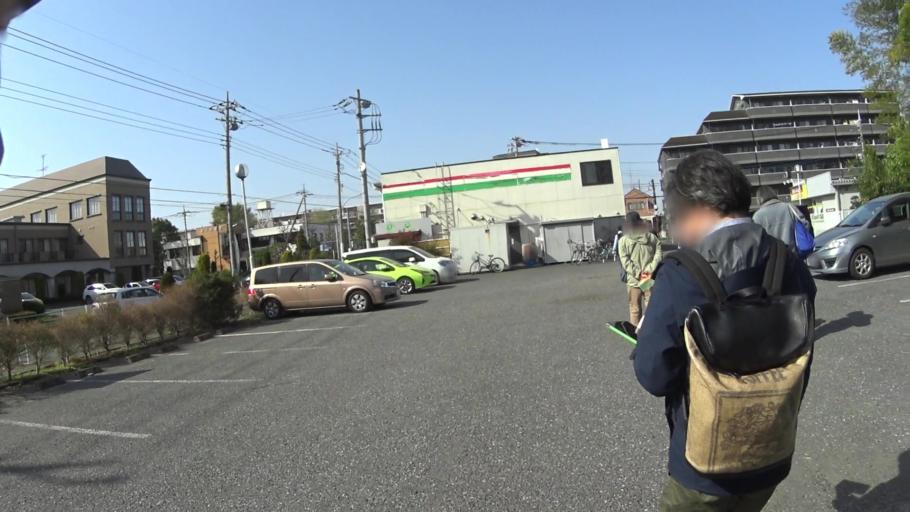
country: JP
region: Tokyo
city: Kokubunji
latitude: 35.7165
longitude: 139.4915
